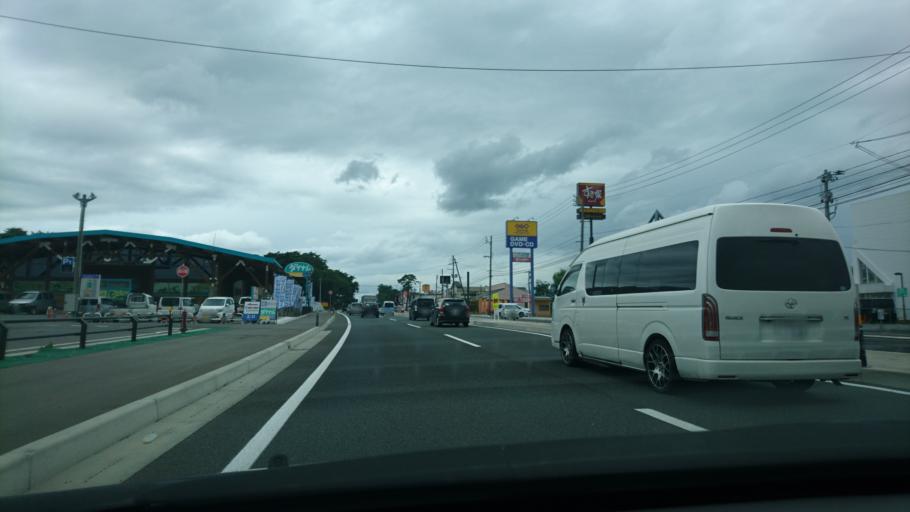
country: JP
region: Iwate
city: Morioka-shi
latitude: 39.7707
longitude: 141.1301
